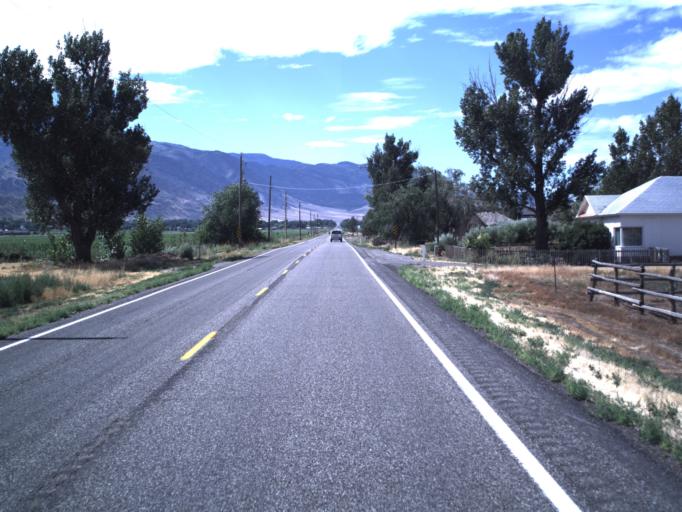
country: US
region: Utah
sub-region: Sevier County
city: Monroe
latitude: 38.6604
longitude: -112.1216
